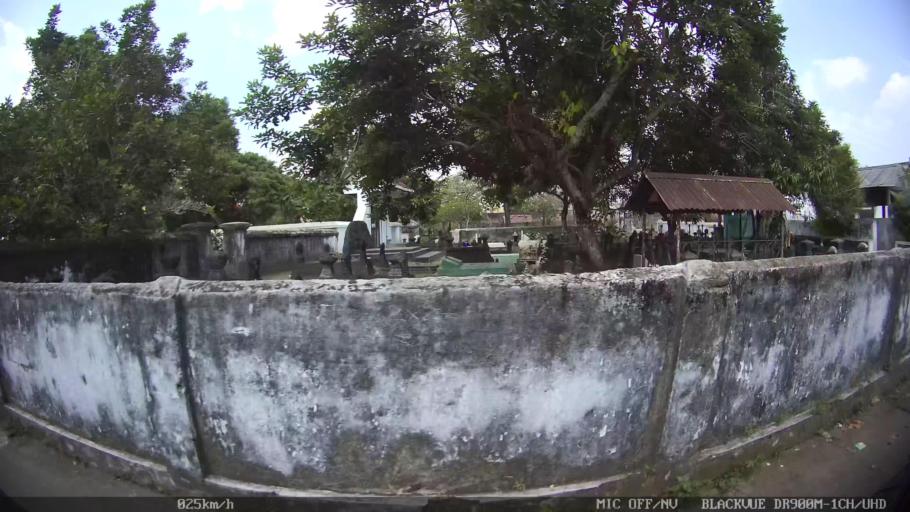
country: ID
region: Daerah Istimewa Yogyakarta
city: Yogyakarta
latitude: -7.8237
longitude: 110.3963
